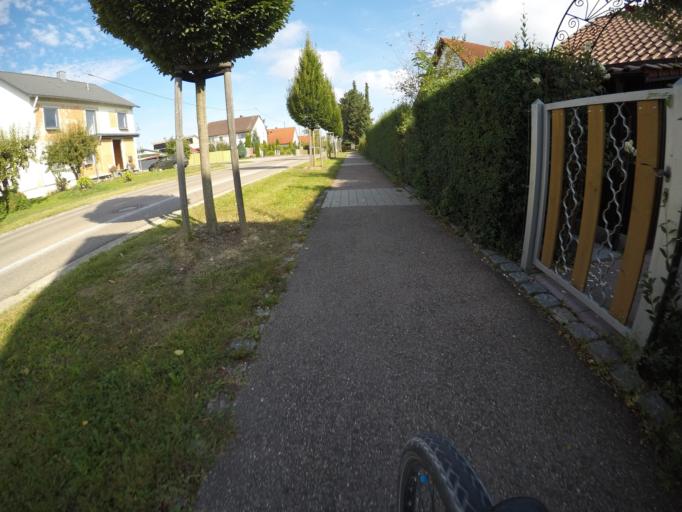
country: DE
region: Bavaria
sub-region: Swabia
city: Allmannshofen
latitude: 48.6101
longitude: 10.8045
